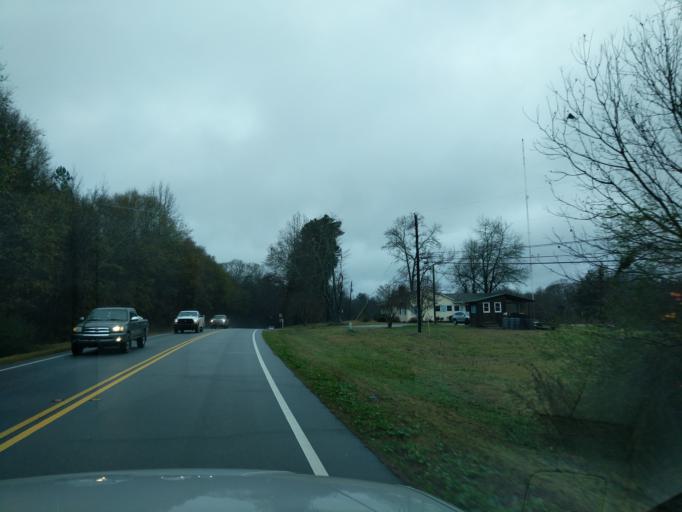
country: US
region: Georgia
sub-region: Franklin County
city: Lavonia
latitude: 34.3701
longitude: -83.0866
